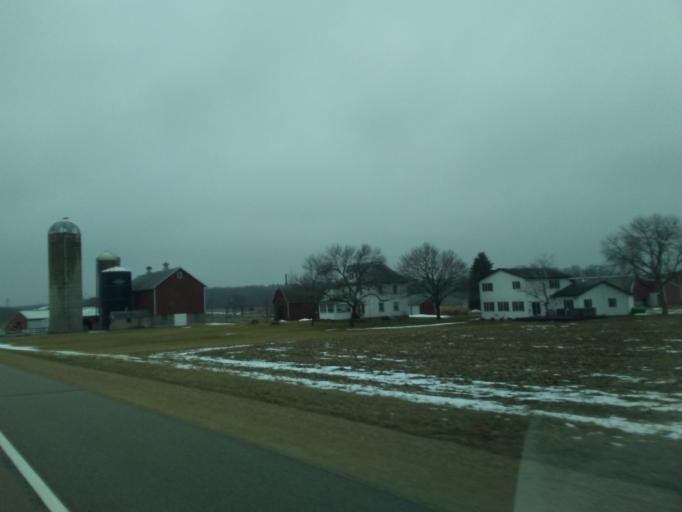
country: US
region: Wisconsin
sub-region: Dane County
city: Mazomanie
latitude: 43.1621
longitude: -89.8448
